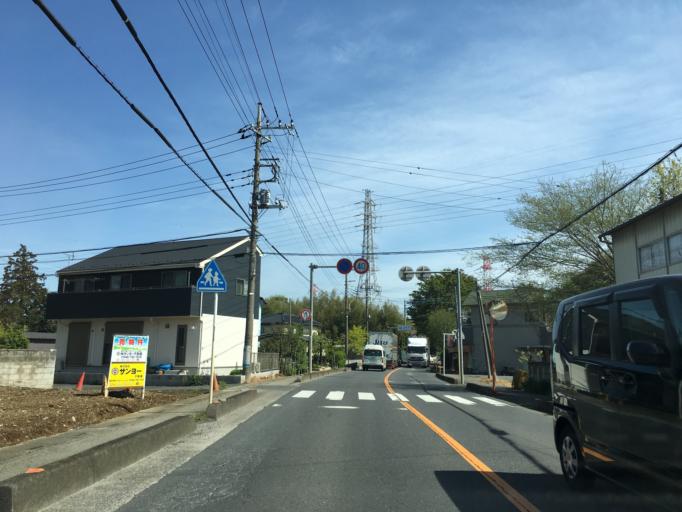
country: JP
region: Saitama
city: Shiraoka
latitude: 36.0011
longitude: 139.6956
